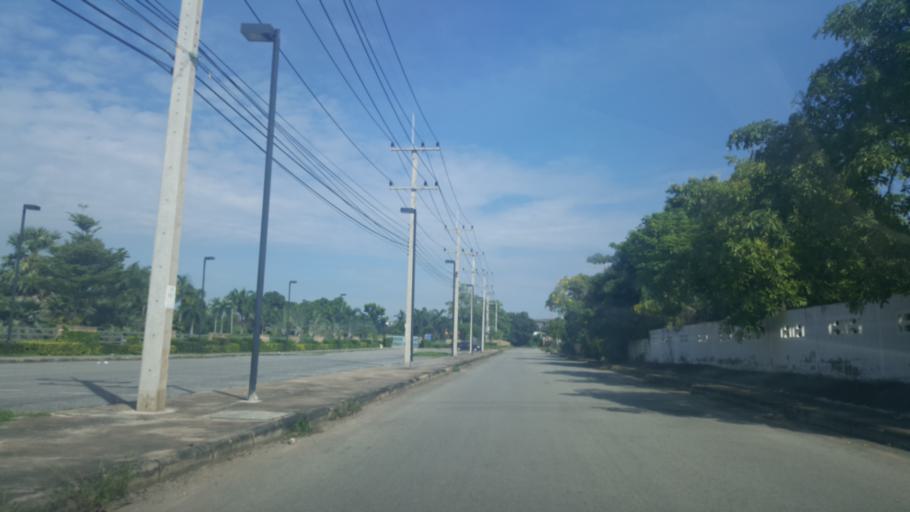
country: TH
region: Chon Buri
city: Sattahip
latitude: 12.6690
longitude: 100.9015
